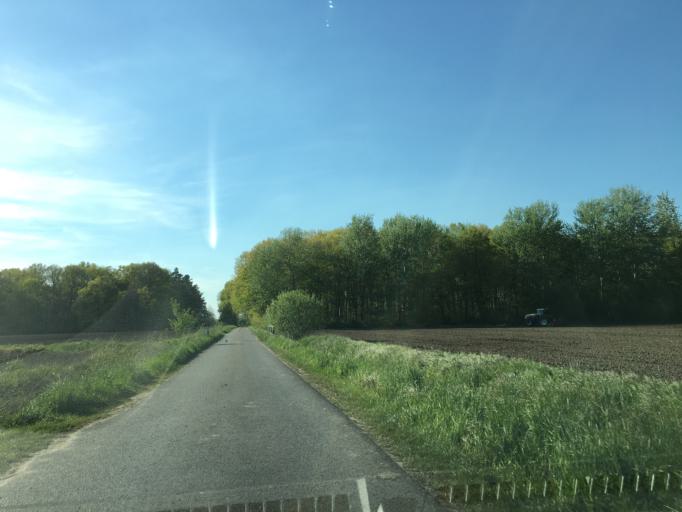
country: DE
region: North Rhine-Westphalia
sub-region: Regierungsbezirk Munster
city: Nordkirchen
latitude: 51.7603
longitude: 7.4953
